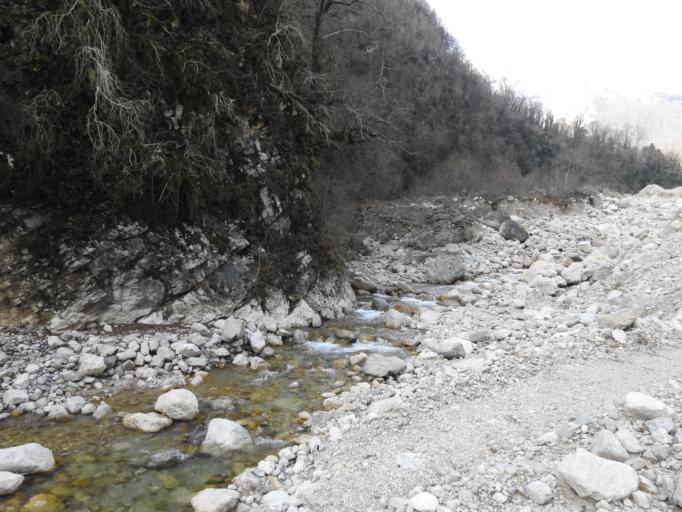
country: GE
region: Abkhazia
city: Gudauta
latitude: 43.2498
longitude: 40.6587
